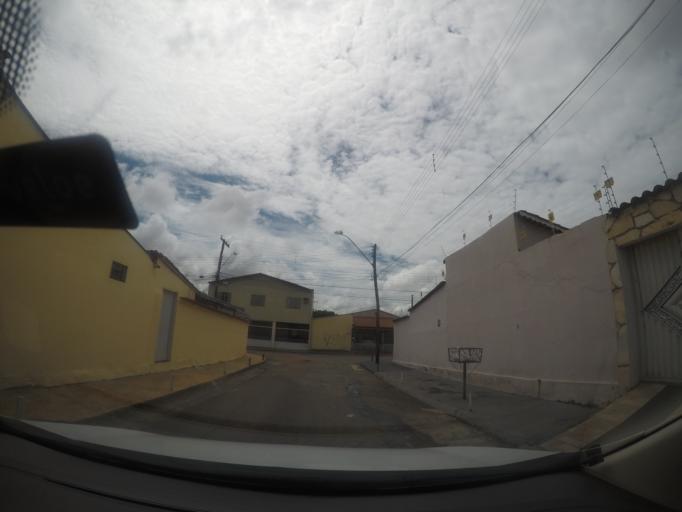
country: BR
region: Goias
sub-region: Goiania
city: Goiania
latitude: -16.6630
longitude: -49.2999
